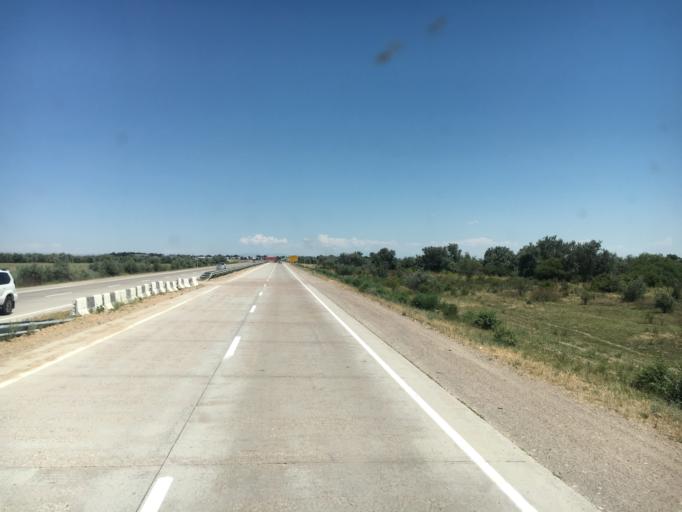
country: KG
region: Chuy
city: Sokuluk
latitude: 43.2678
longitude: 74.2101
